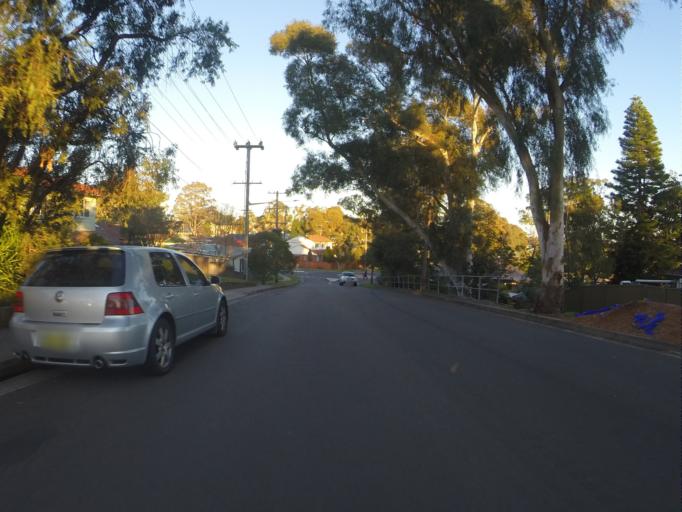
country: AU
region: New South Wales
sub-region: Sutherland Shire
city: Engadine
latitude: -34.0578
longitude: 151.0116
